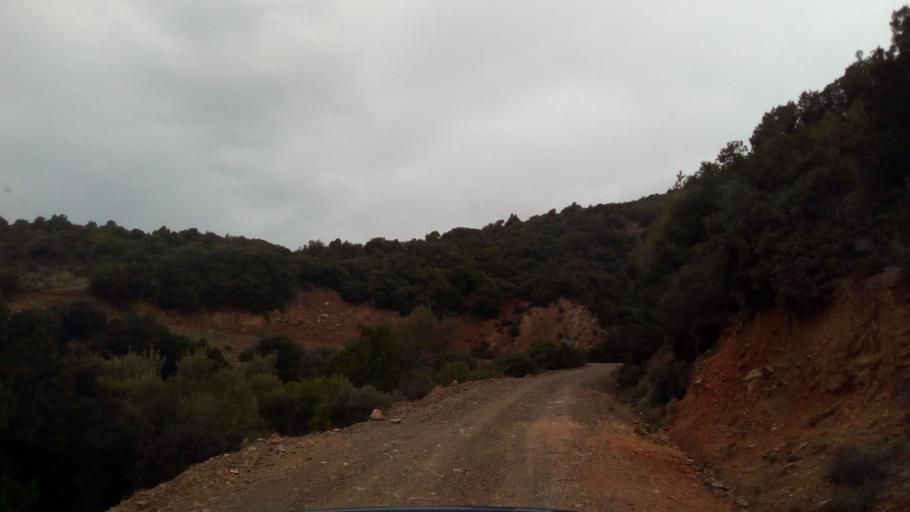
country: GR
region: West Greece
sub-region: Nomos Achaias
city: Temeni
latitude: 38.3697
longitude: 22.1584
